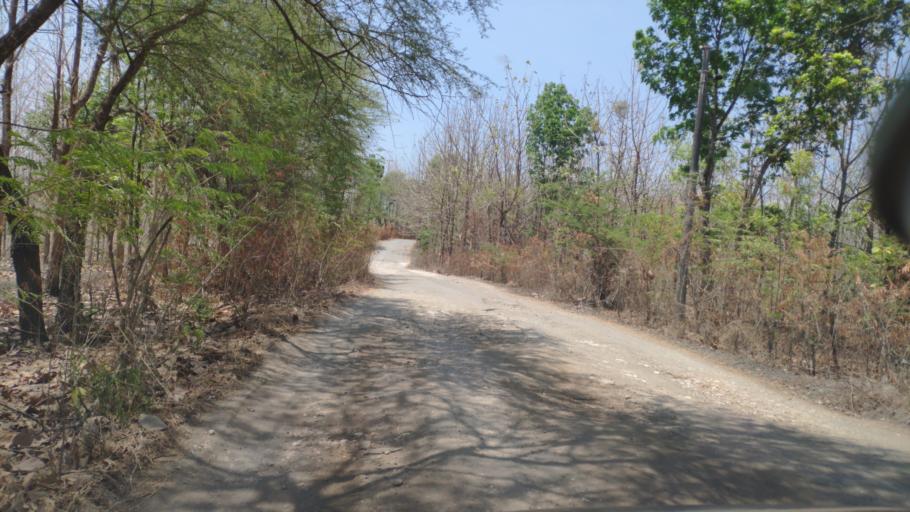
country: ID
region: Central Java
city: Randublatung
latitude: -7.2427
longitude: 111.3803
